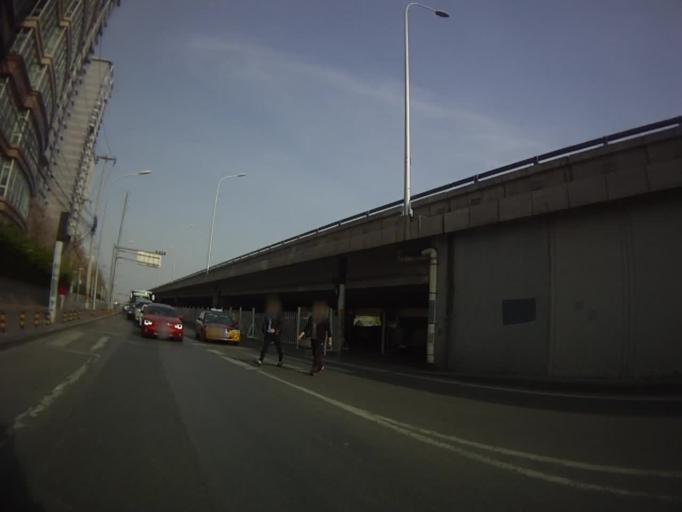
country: CN
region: Beijing
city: Chaowai
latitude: 39.9025
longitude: 116.4424
